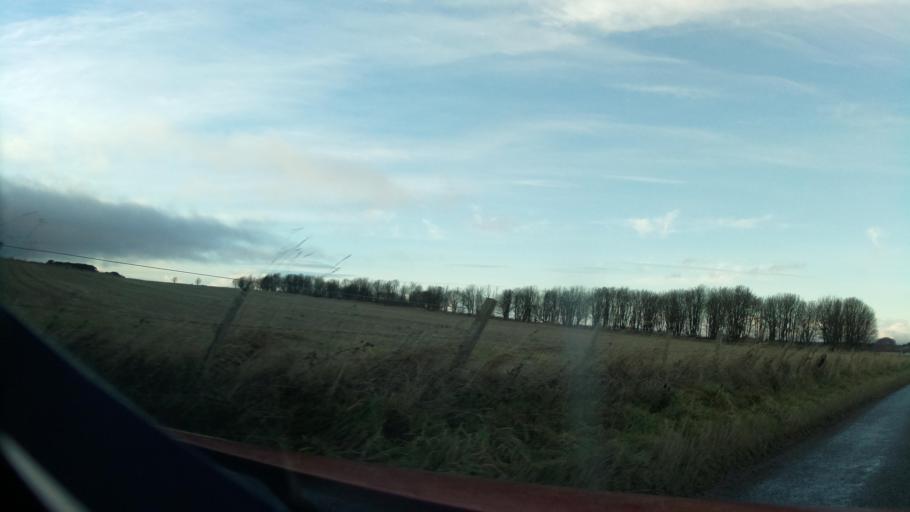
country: GB
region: Scotland
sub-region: Angus
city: Letham
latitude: 56.5653
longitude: -2.7746
